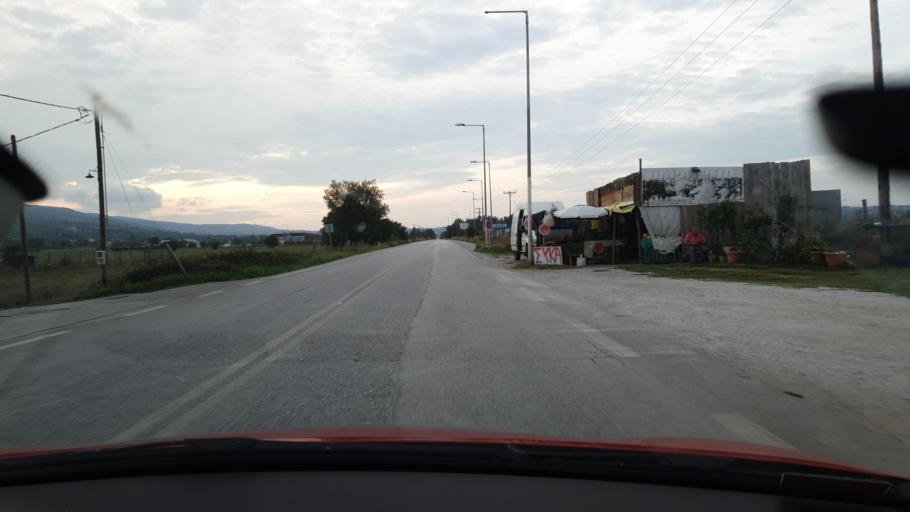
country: GR
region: Central Macedonia
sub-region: Nomos Thessalonikis
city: Liti
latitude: 40.7532
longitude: 22.9862
